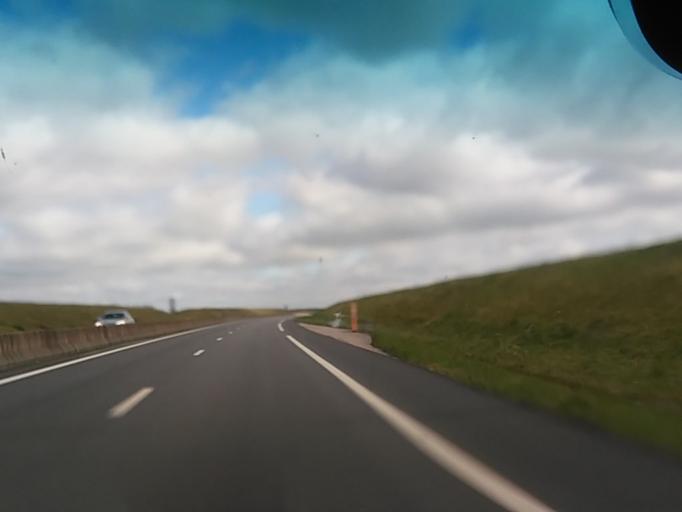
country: FR
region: Haute-Normandie
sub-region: Departement de l'Eure
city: Brionne
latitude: 49.1795
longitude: 0.7499
